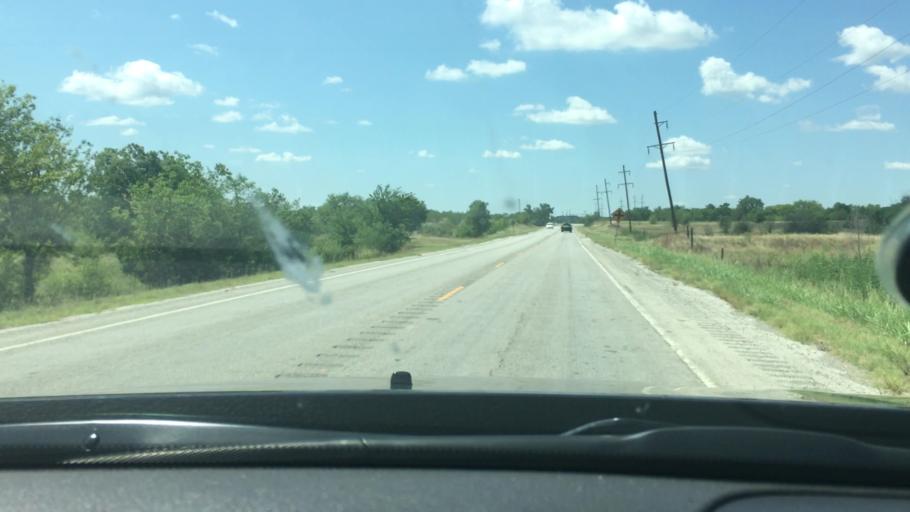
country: US
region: Oklahoma
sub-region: Carter County
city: Ardmore
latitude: 34.0763
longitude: -97.1429
